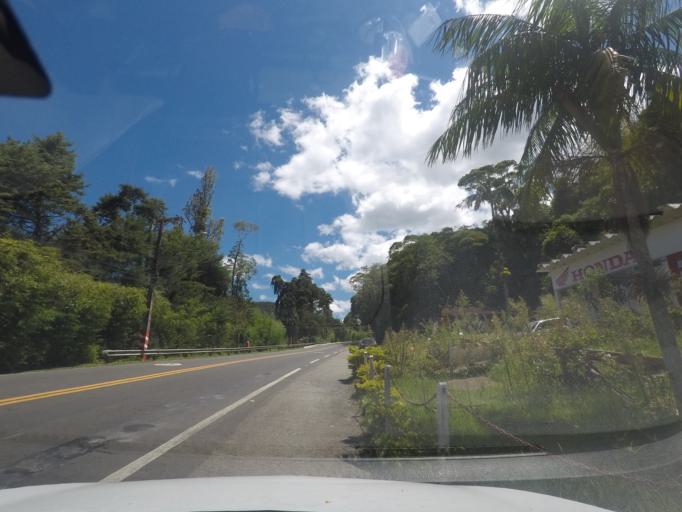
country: BR
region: Rio de Janeiro
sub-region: Teresopolis
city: Teresopolis
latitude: -22.4516
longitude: -42.9823
